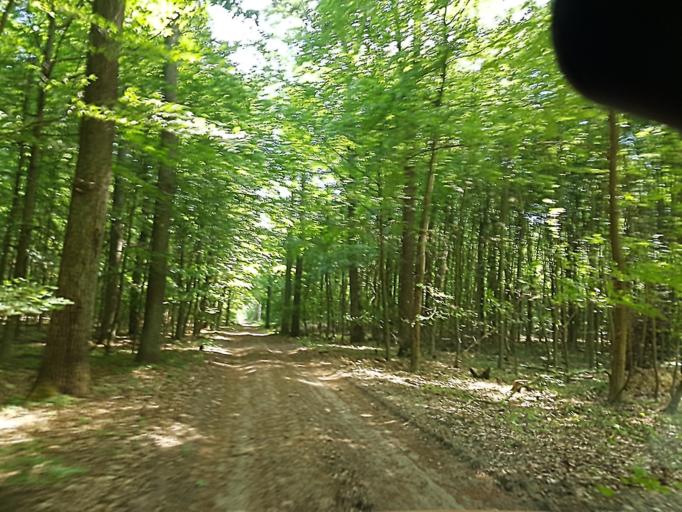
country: DE
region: Brandenburg
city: Gorzke
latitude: 52.0974
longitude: 12.3101
